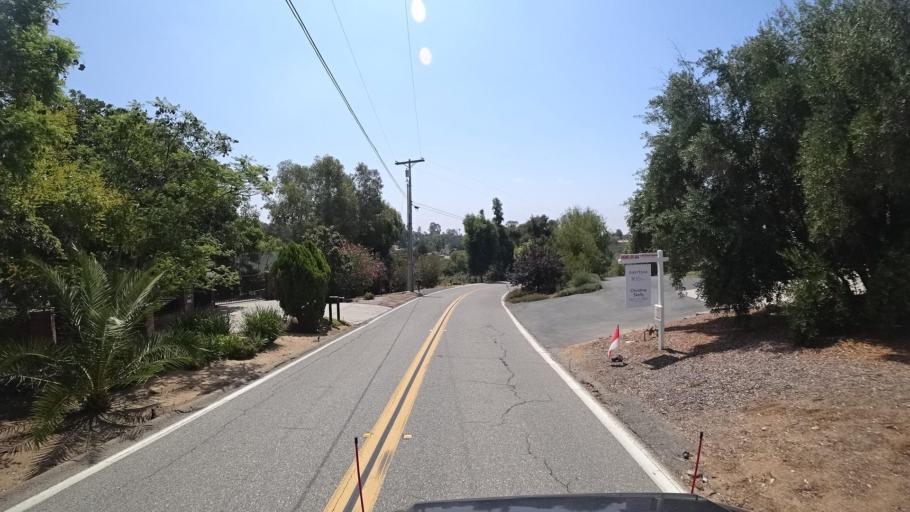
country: US
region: California
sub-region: San Diego County
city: Fallbrook
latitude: 33.3383
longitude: -117.2269
